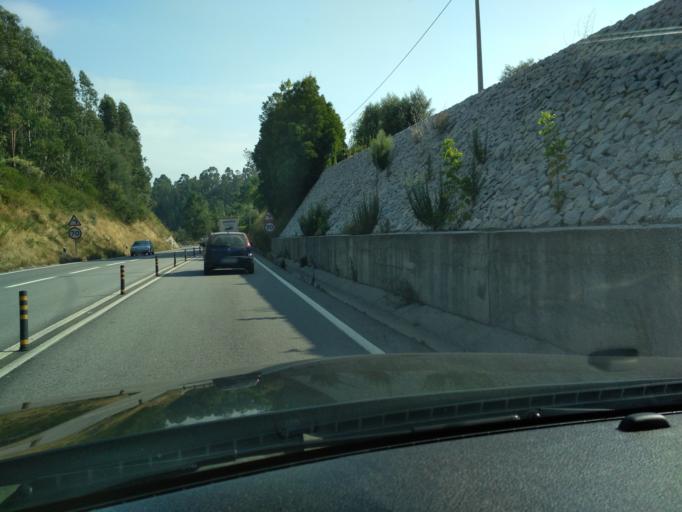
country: PT
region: Aveiro
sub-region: Mealhada
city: Pampilhosa do Botao
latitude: 40.2807
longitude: -8.4459
